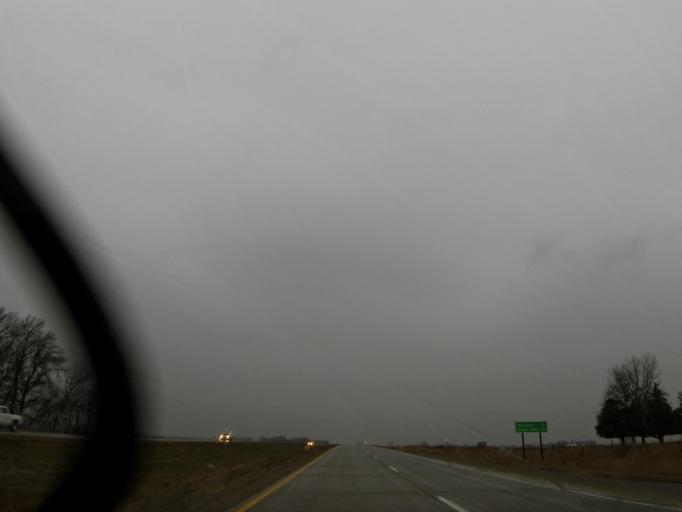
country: US
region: Iowa
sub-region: Cerro Gordo County
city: Mason City
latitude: 43.1120
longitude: -93.1404
